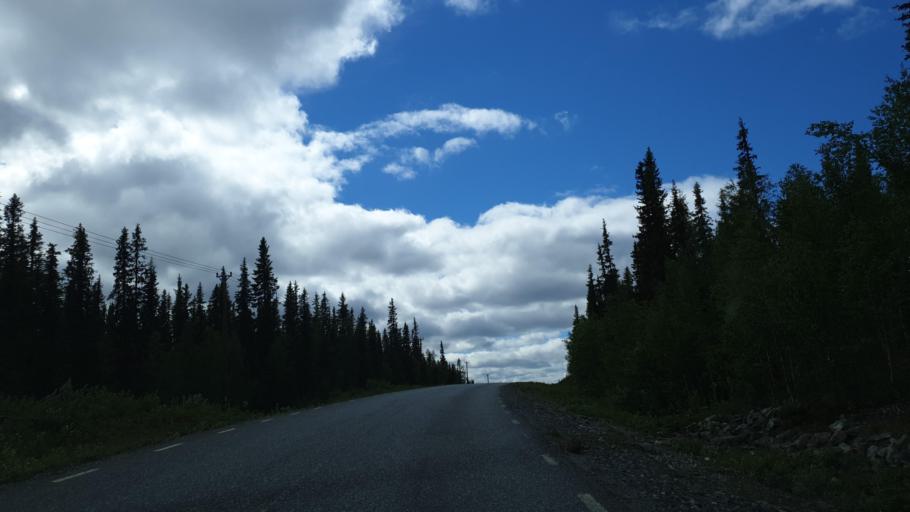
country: SE
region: Vaesterbotten
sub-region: Vilhelmina Kommun
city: Sjoberg
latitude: 65.1876
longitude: 15.9432
